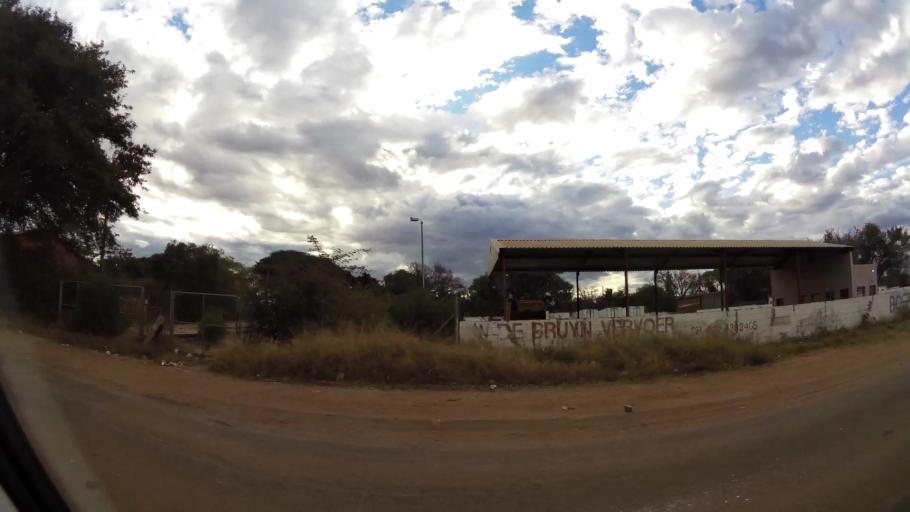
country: ZA
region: Limpopo
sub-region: Waterberg District Municipality
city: Modimolle
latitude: -24.5189
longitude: 28.7184
